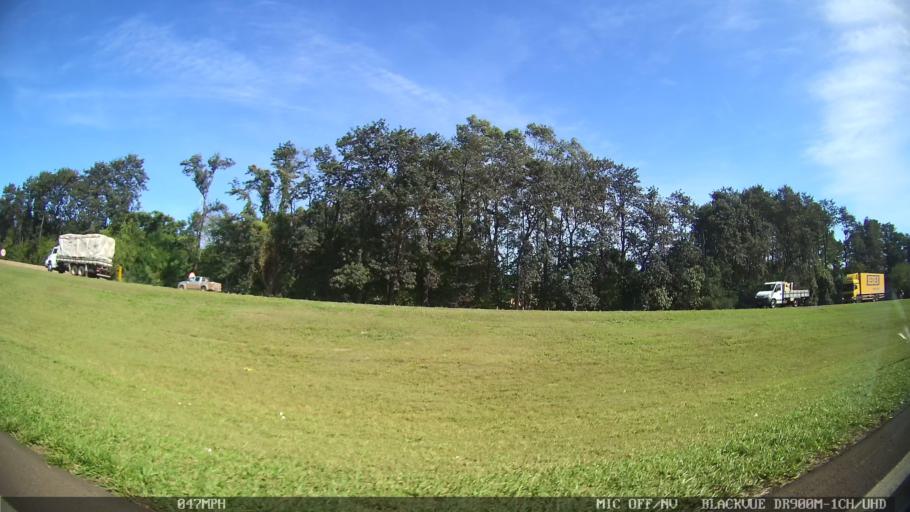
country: BR
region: Sao Paulo
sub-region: Leme
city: Leme
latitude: -22.2448
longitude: -47.3903
